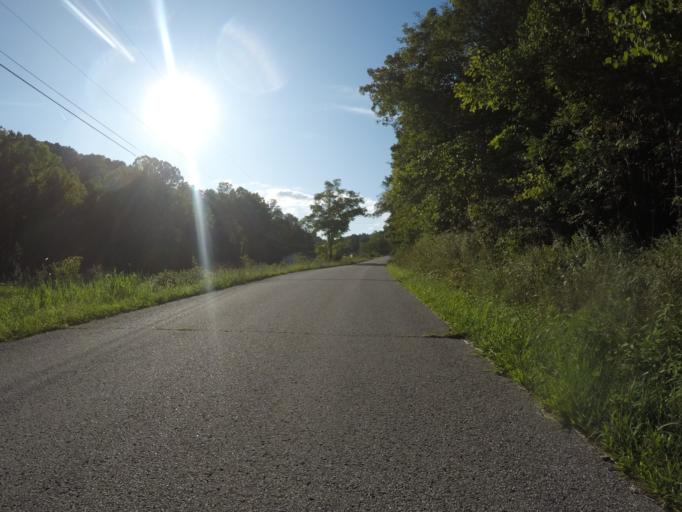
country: US
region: Ohio
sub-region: Lawrence County
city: Burlington
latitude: 38.5222
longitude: -82.5056
